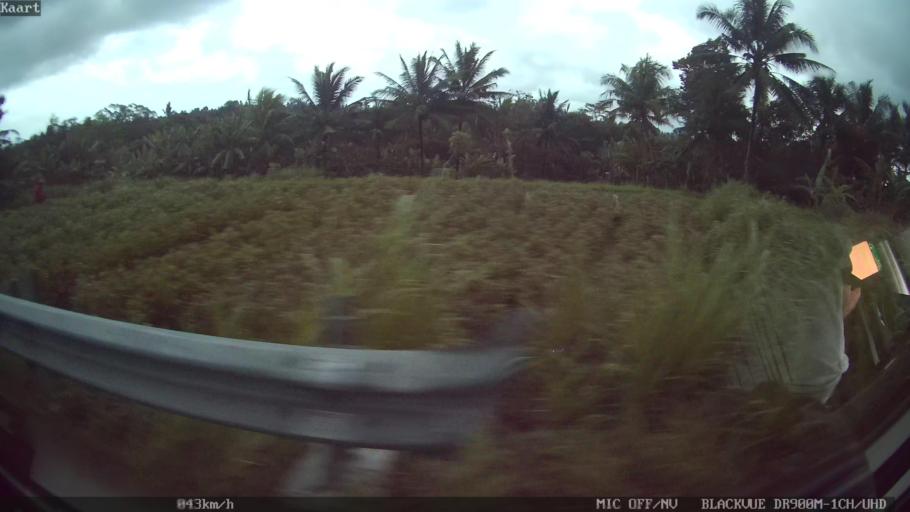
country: ID
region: Bali
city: Banjar Sempidi
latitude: -8.5183
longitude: 115.1957
